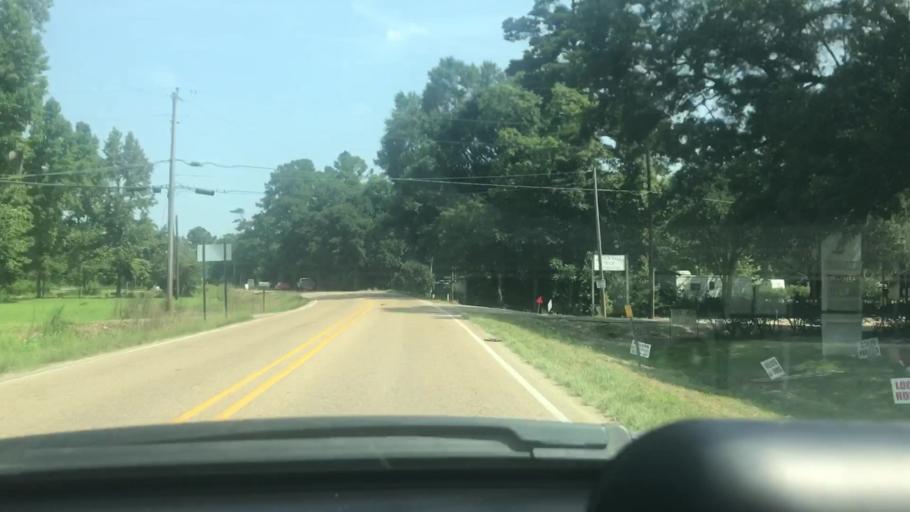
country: US
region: Louisiana
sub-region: Livingston Parish
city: Denham Springs
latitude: 30.4762
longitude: -90.9184
